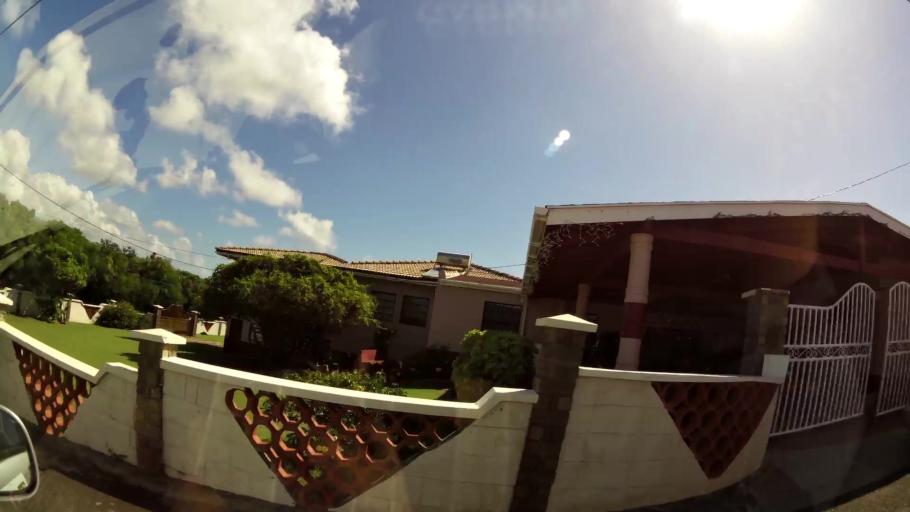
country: GD
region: Saint George
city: Saint George's
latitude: 11.9896
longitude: -61.7604
